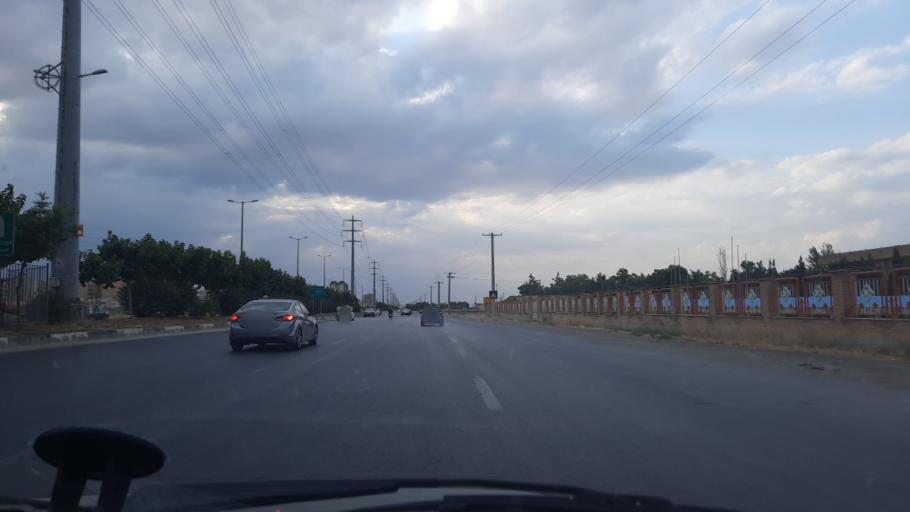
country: IR
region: Markazi
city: Arak
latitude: 34.1008
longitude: 49.7507
